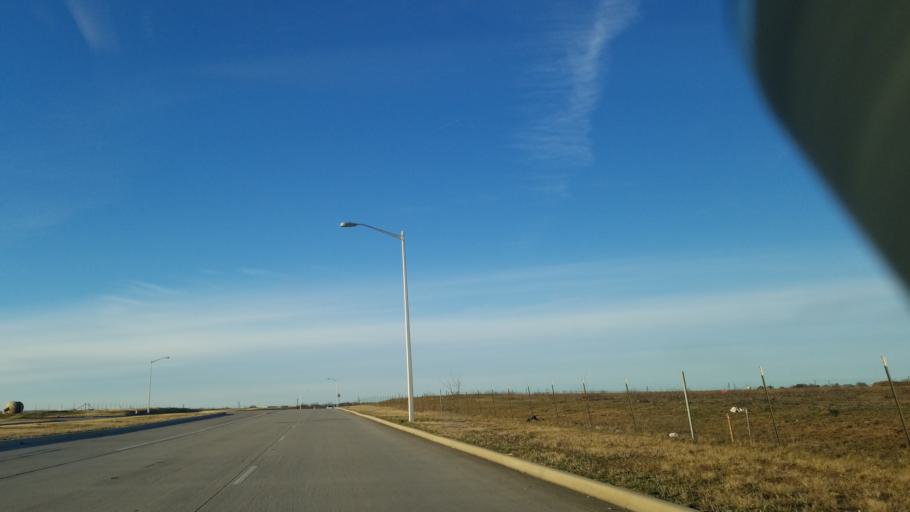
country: US
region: Texas
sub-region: Denton County
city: Denton
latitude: 33.2142
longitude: -97.1847
